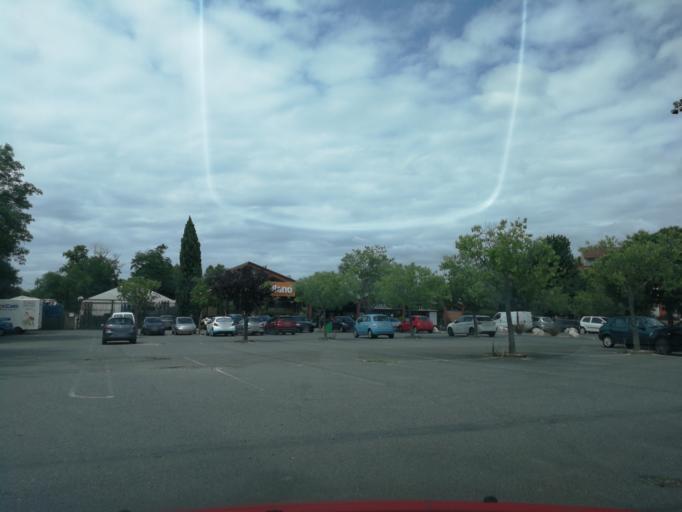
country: FR
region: Midi-Pyrenees
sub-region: Departement de la Haute-Garonne
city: Ramonville-Saint-Agne
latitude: 43.5689
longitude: 1.4993
